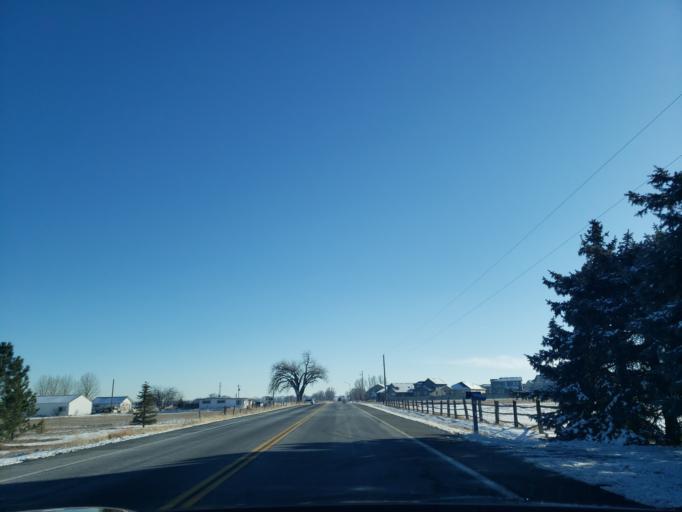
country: US
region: Colorado
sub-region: Weld County
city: Windsor
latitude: 40.5105
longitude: -105.0008
